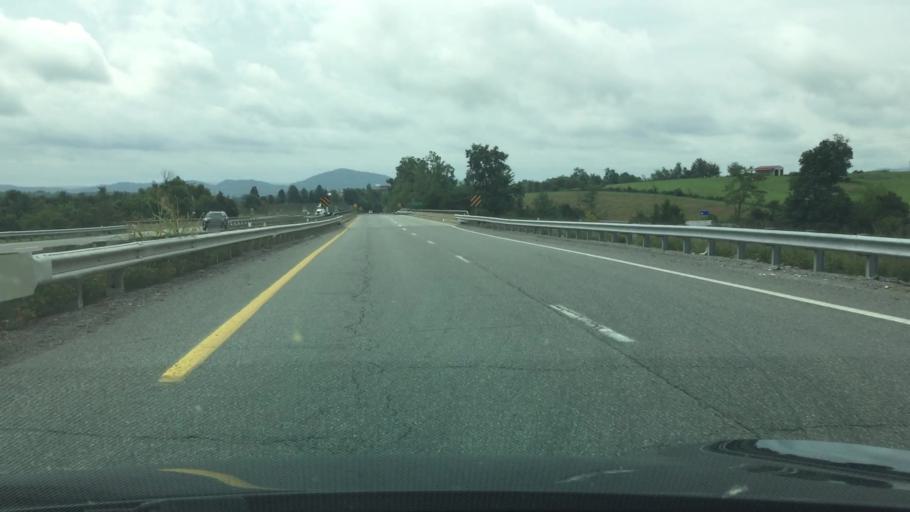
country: US
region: Virginia
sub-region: City of Radford
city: Radford
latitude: 37.0974
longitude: -80.5081
